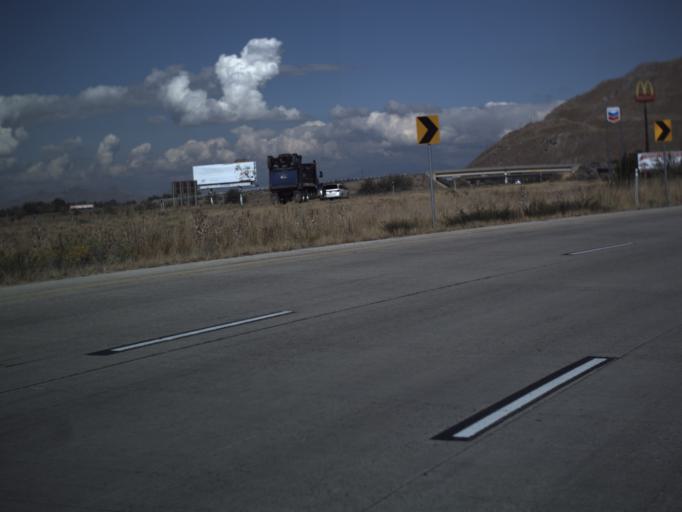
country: US
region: Utah
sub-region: Tooele County
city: Stansbury park
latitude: 40.6859
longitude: -112.2707
